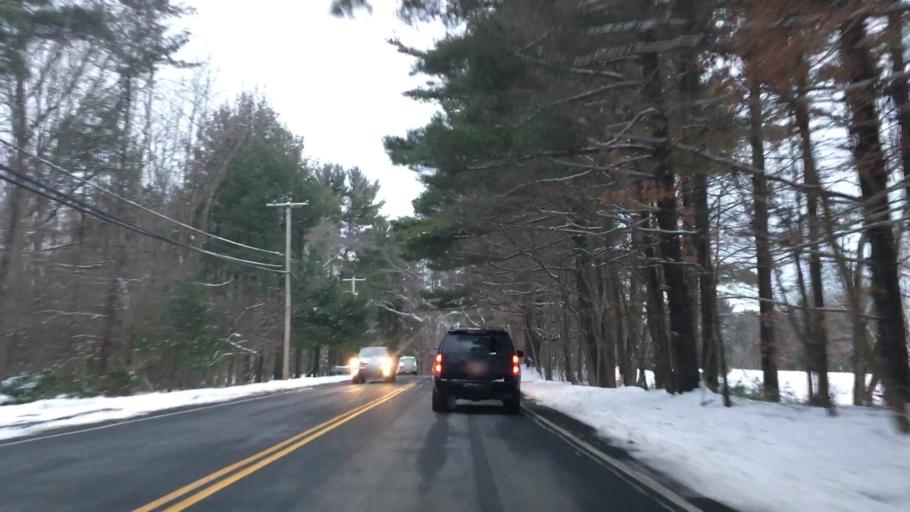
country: US
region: Massachusetts
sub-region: Hampden County
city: Longmeadow
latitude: 42.0444
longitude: -72.5721
